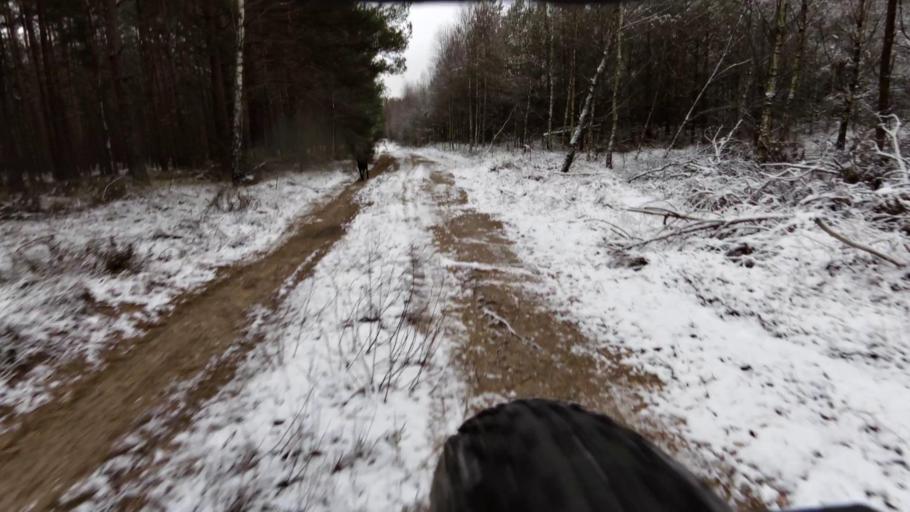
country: PL
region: West Pomeranian Voivodeship
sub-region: Powiat walecki
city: Miroslawiec
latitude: 53.3799
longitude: 16.1119
